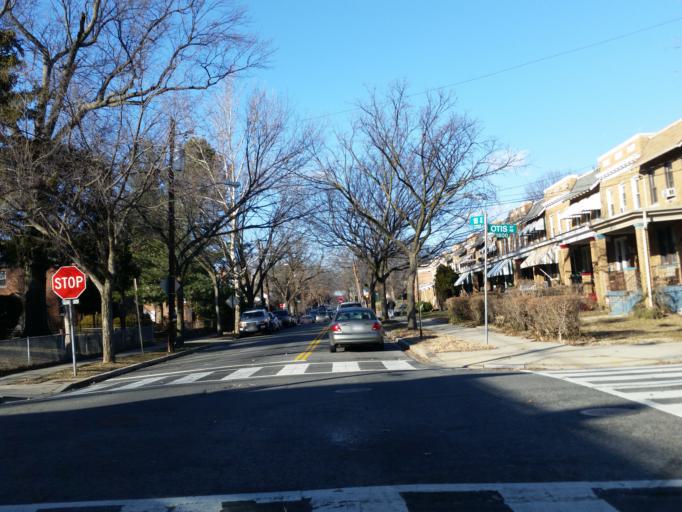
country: US
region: Maryland
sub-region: Prince George's County
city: Mount Rainier
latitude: 38.9350
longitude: -76.9797
